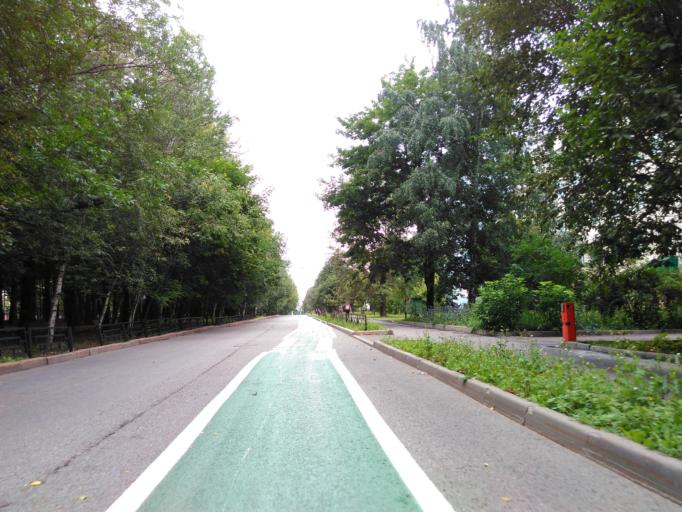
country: RU
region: Moscow
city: Vorob'yovo
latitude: 55.6961
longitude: 37.5335
